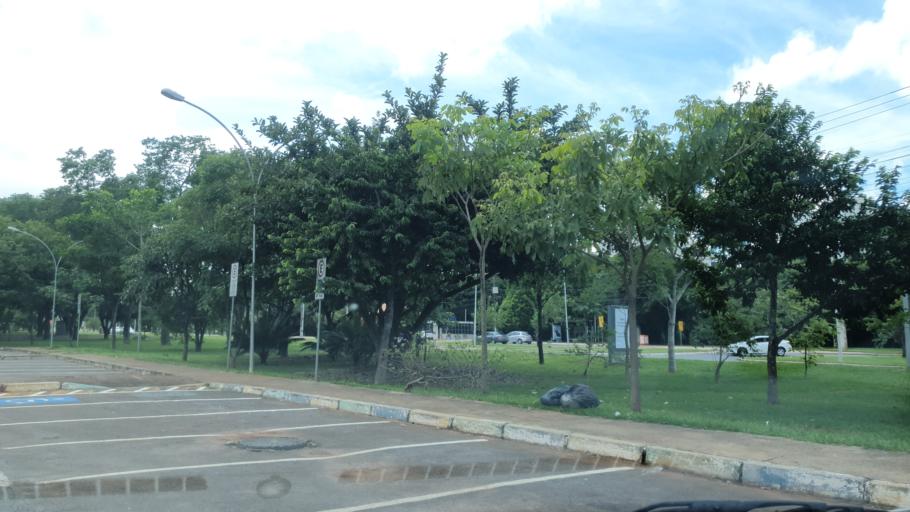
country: BR
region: Federal District
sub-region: Brasilia
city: Brasilia
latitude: -15.8004
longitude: -47.9443
